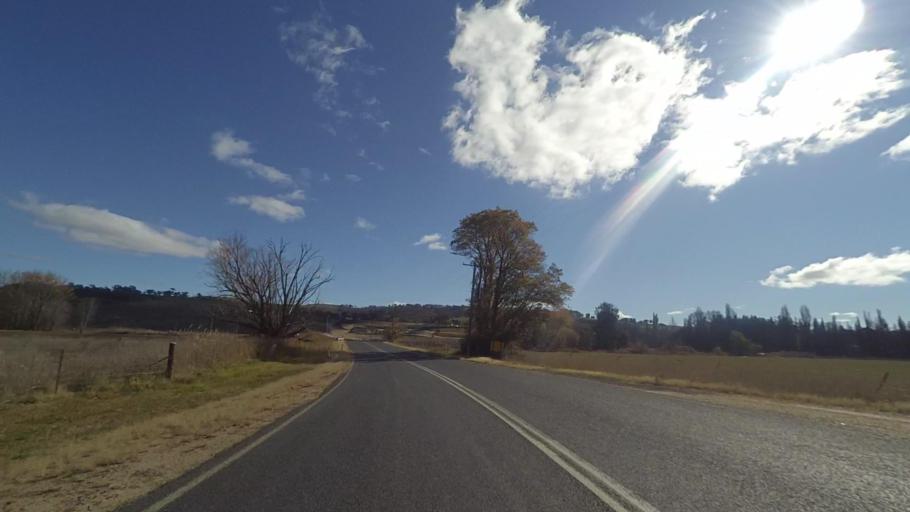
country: AU
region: New South Wales
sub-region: Bathurst Regional
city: Perthville
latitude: -33.4667
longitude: 149.5727
